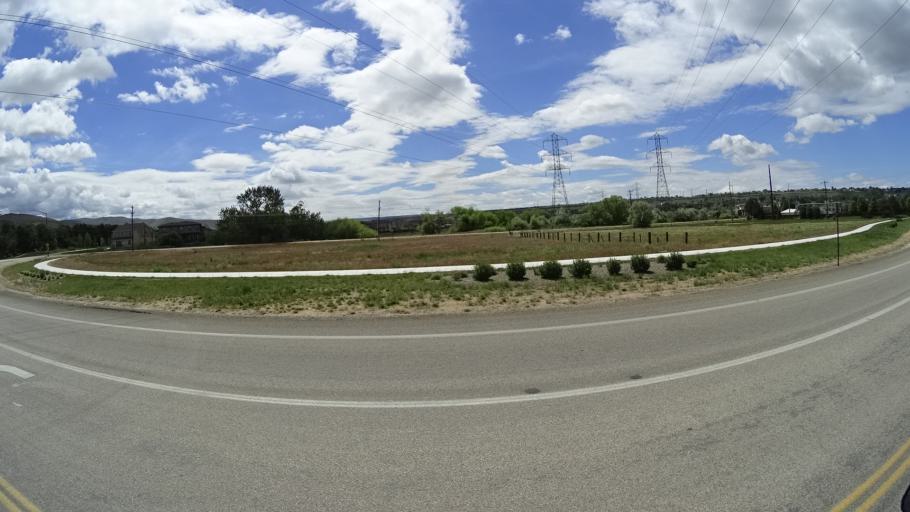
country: US
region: Idaho
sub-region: Ada County
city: Boise
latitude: 43.5713
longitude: -116.1257
